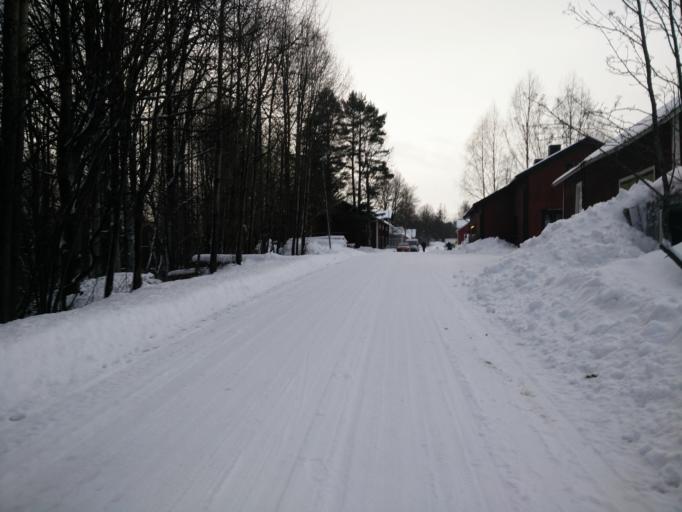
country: SE
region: Vaesternorrland
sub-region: Sundsvalls Kommun
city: Kvissleby
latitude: 62.2929
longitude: 17.3779
